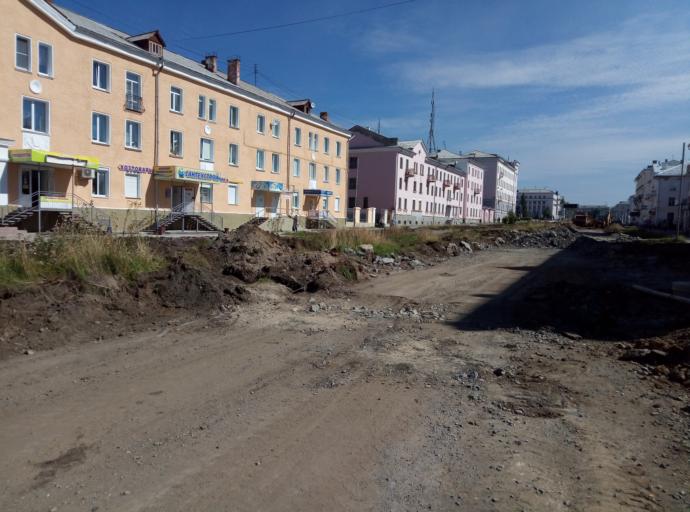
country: RU
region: Sverdlovsk
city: Krasnotur'insk
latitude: 59.7637
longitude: 60.1883
